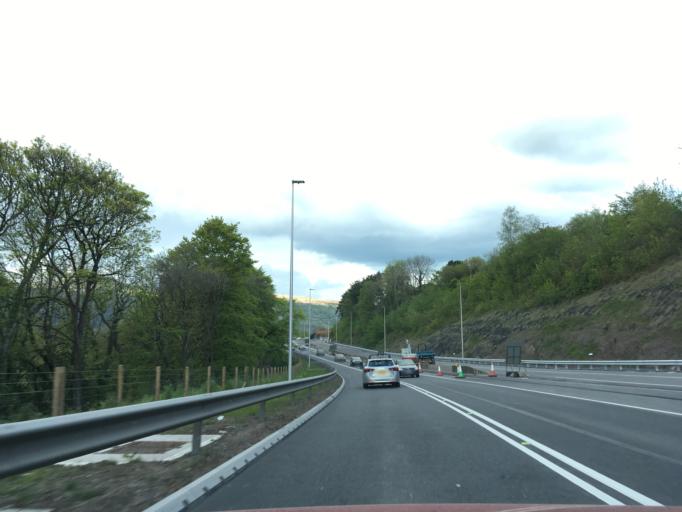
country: GB
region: Wales
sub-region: Monmouthshire
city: Gilwern
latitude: 51.8211
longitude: -3.1021
